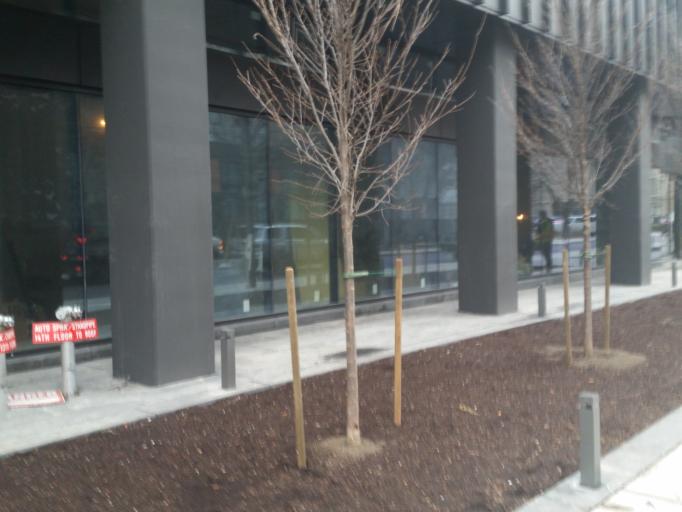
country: CA
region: Ontario
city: Toronto
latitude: 43.6697
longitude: -79.3799
